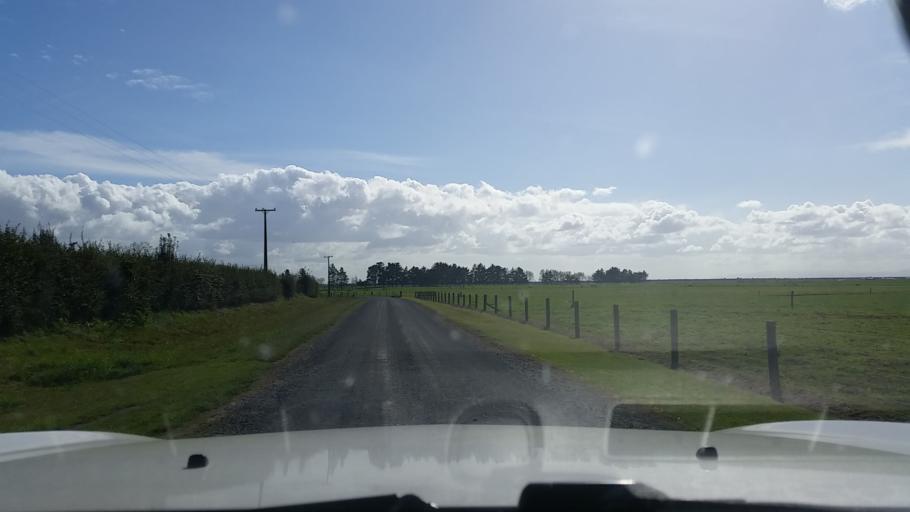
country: NZ
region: Waikato
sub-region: Hauraki District
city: Paeroa
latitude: -37.5073
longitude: 175.5883
